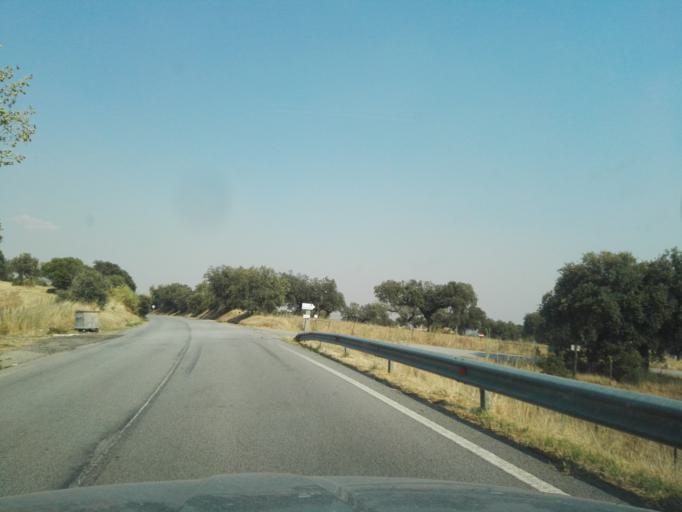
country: PT
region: Portalegre
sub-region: Campo Maior
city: Campo Maior
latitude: 38.9932
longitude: -7.1554
